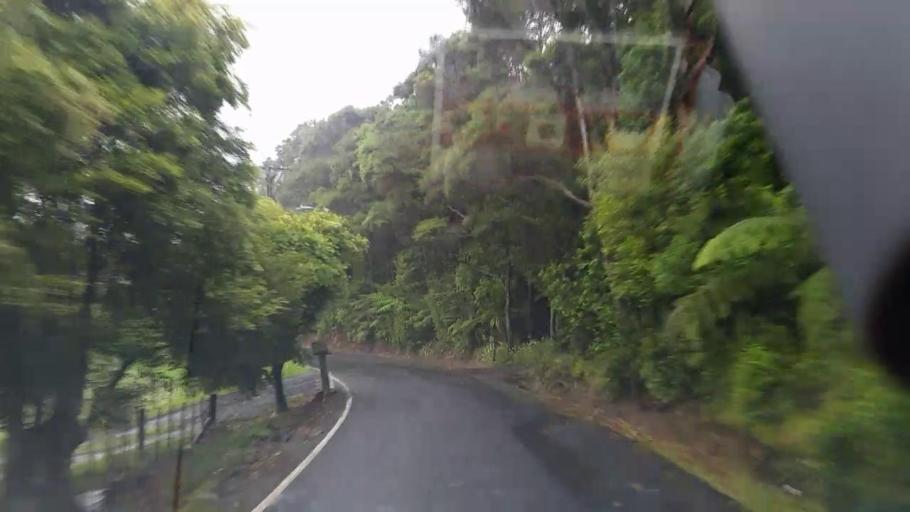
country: NZ
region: Auckland
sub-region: Auckland
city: Waitakere
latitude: -36.9126
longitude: 174.5671
